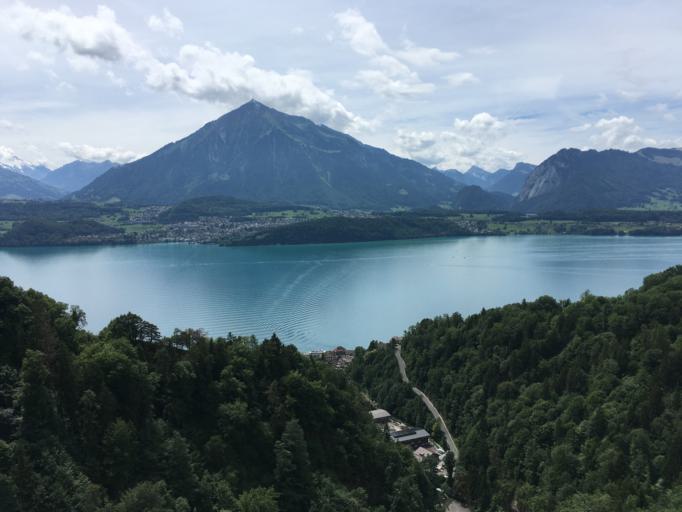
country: CH
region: Bern
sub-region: Thun District
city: Sigriswil
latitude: 46.7189
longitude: 7.7064
